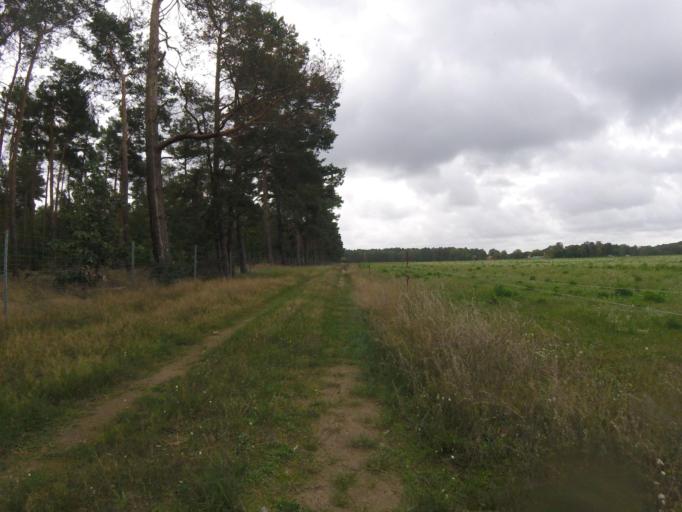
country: DE
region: Brandenburg
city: Gross Koris
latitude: 52.1832
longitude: 13.6734
